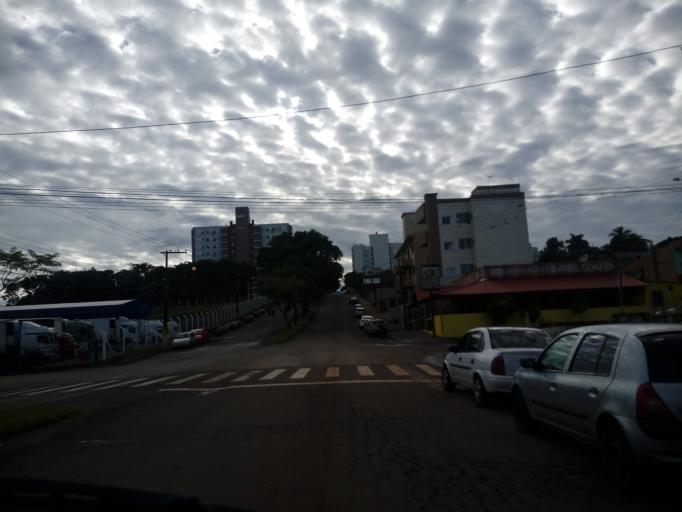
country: BR
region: Santa Catarina
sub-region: Chapeco
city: Chapeco
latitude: -27.1058
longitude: -52.6275
